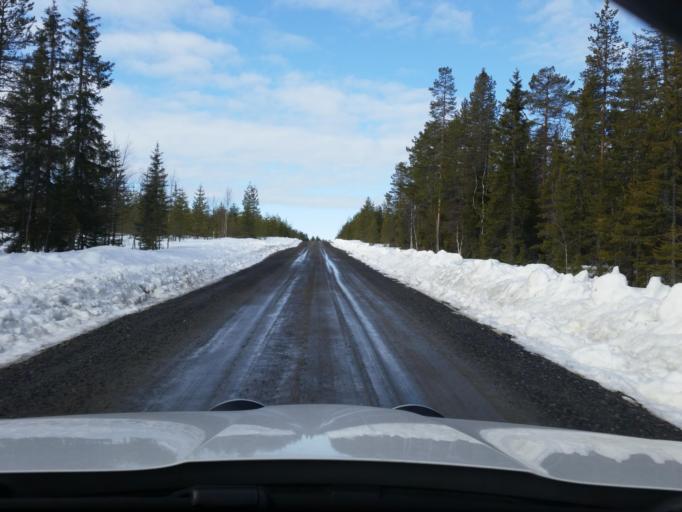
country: SE
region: Vaesterbotten
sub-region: Skelleftea Kommun
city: Storvik
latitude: 65.5096
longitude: 20.4218
